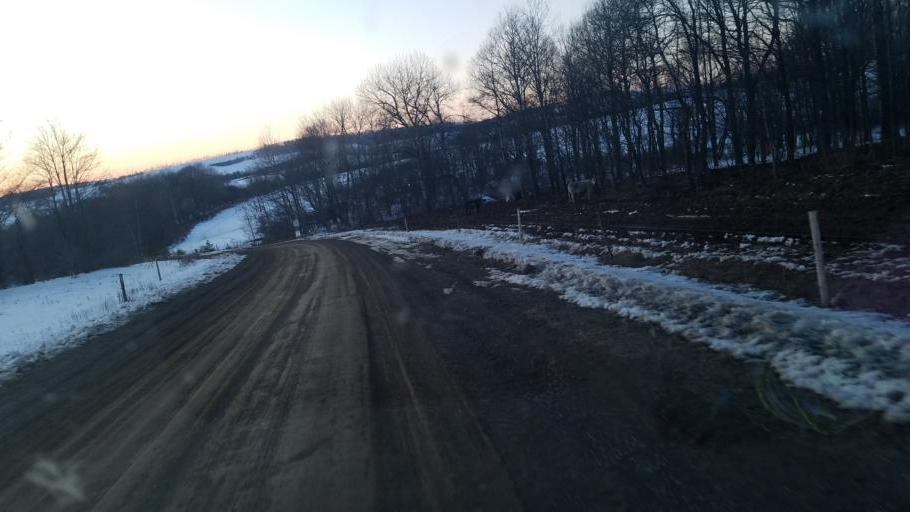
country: US
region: New York
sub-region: Allegany County
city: Andover
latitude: 42.0079
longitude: -77.7487
